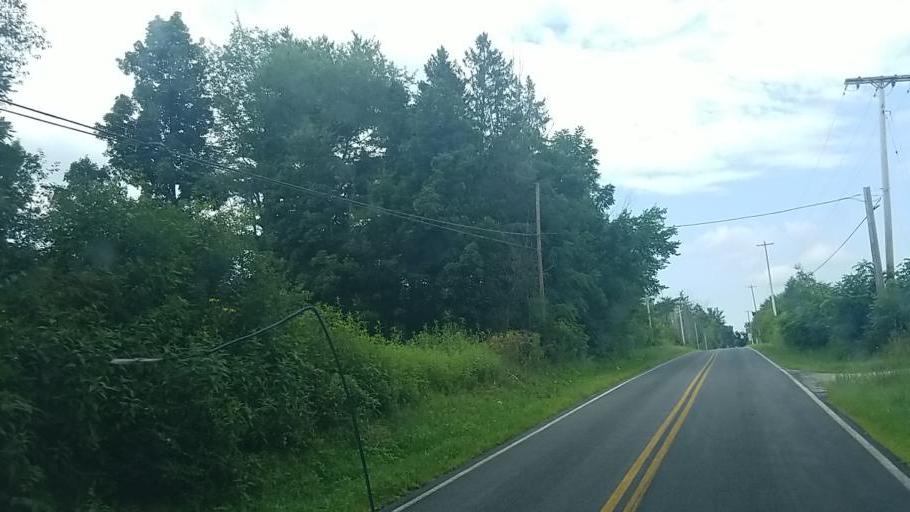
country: US
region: Ohio
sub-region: Medina County
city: Westfield Center
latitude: 41.0200
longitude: -81.9416
